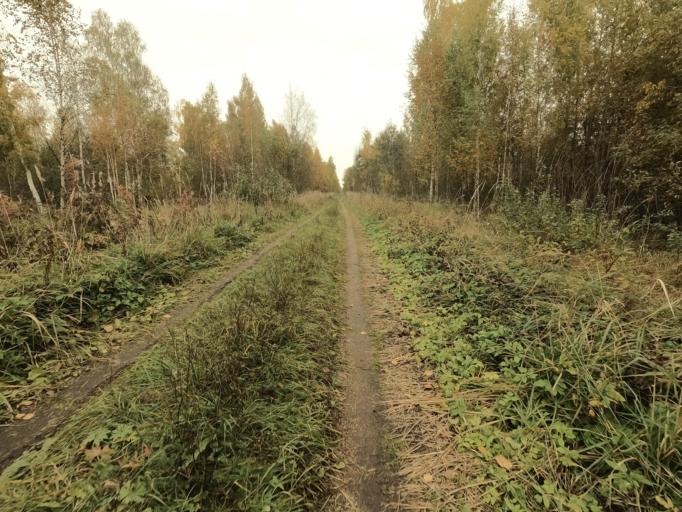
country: RU
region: Novgorod
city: Pankovka
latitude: 58.8803
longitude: 30.9429
